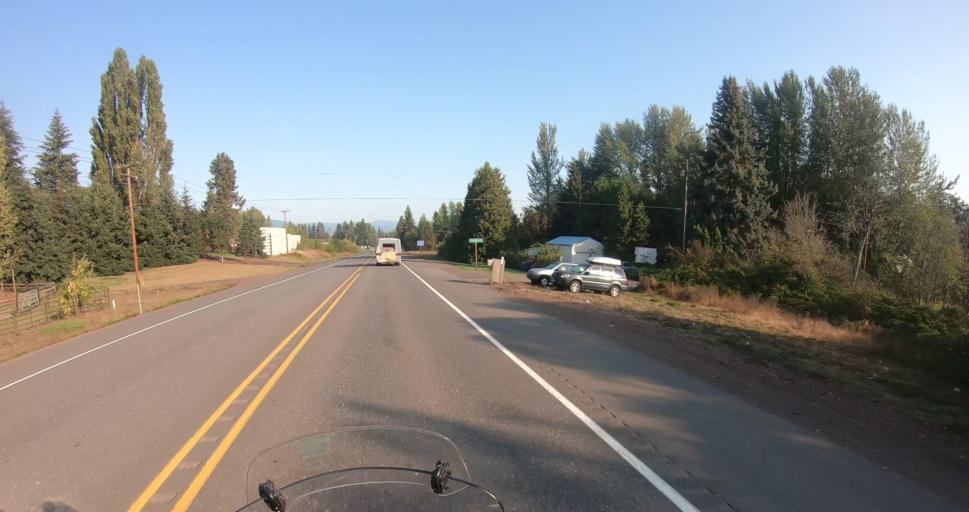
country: US
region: Oregon
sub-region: Hood River County
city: Odell
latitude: 45.6356
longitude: -121.5129
